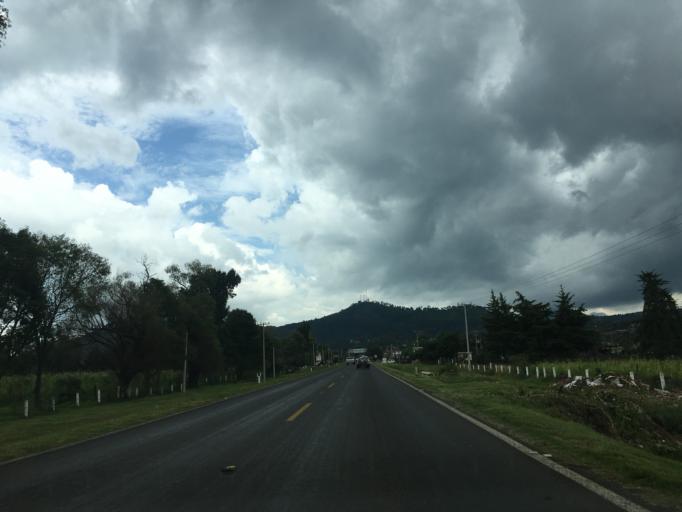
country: MX
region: Michoacan
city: Patzcuaro
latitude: 19.5325
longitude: -101.6263
